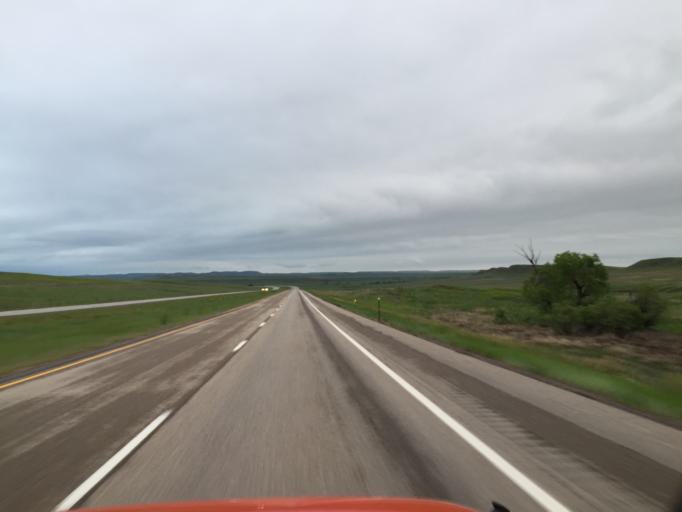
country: US
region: South Dakota
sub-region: Fall River County
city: Hot Springs
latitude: 43.5501
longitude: -103.3198
